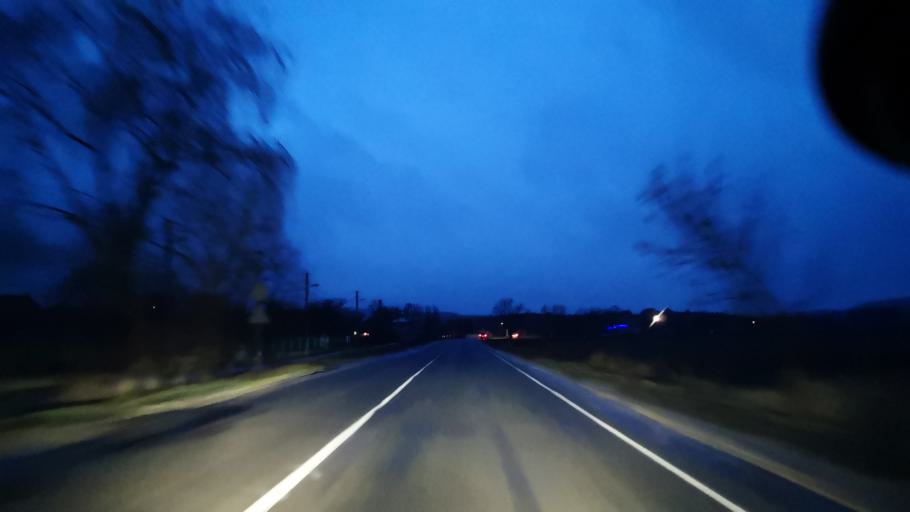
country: MD
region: Orhei
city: Orhei
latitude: 47.4571
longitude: 28.7908
